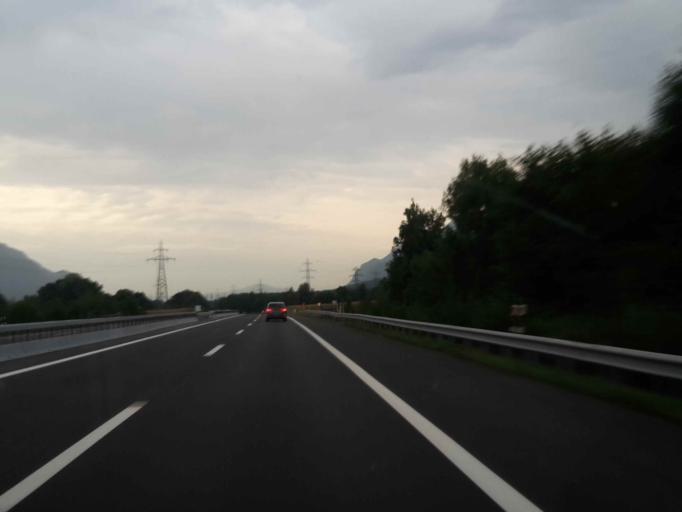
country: CH
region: Vaud
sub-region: Aigle District
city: Bex
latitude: 46.2454
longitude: 6.9941
